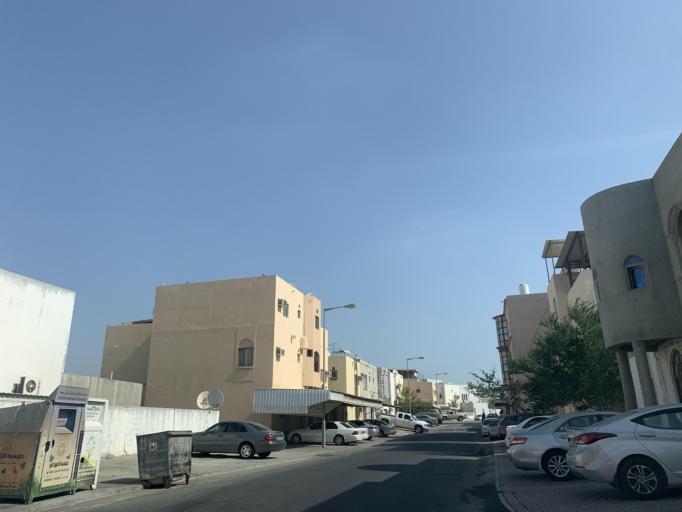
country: BH
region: Central Governorate
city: Madinat Hamad
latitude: 26.1288
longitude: 50.4999
